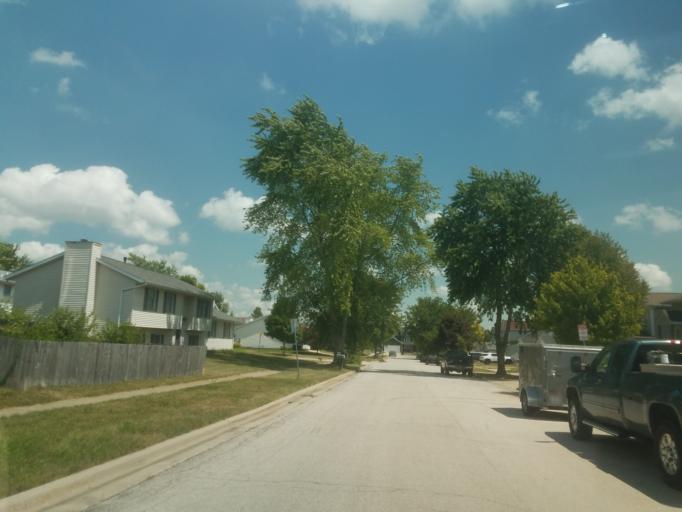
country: US
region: Illinois
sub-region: McLean County
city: Bloomington
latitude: 40.4420
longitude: -89.0330
